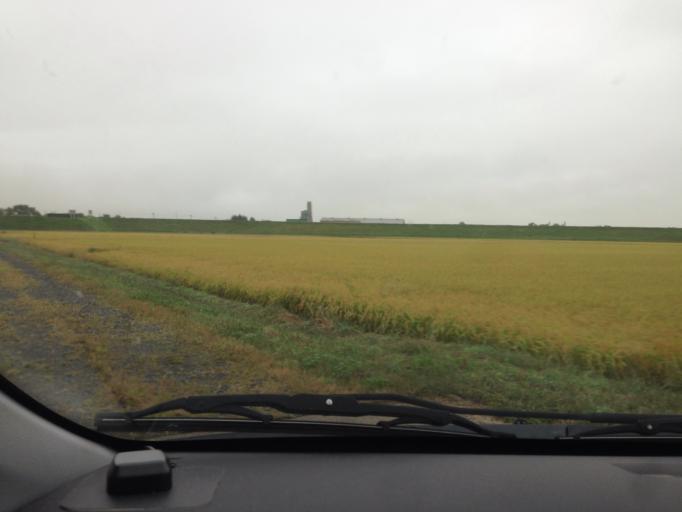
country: JP
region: Fukushima
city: Kitakata
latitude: 37.5907
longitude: 139.8679
